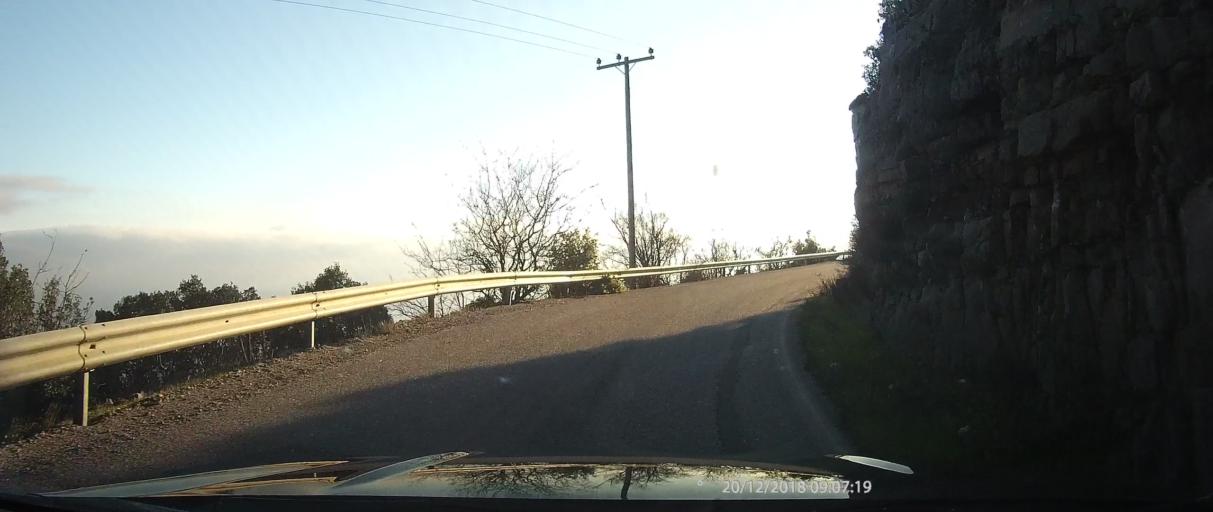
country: GR
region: Peloponnese
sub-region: Nomos Lakonias
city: Sykea
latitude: 36.9279
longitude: 23.0055
